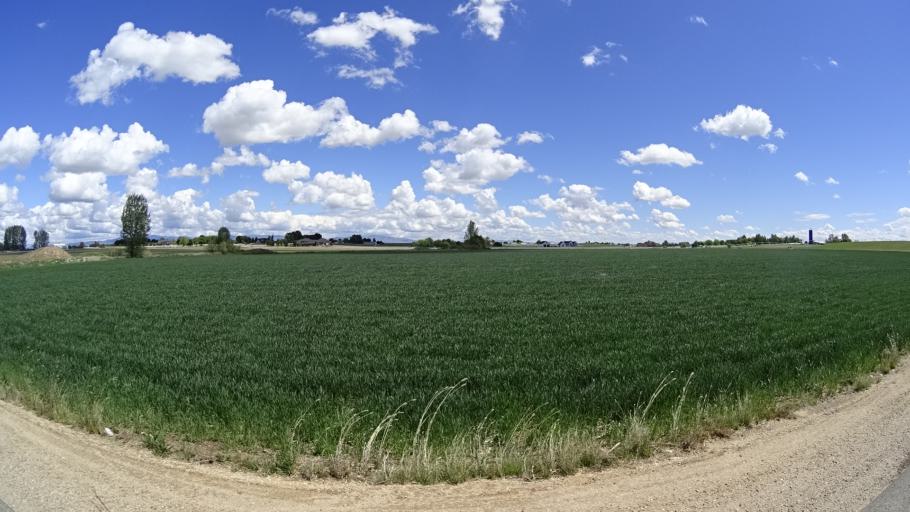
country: US
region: Idaho
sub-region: Ada County
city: Meridian
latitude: 43.5700
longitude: -116.4338
